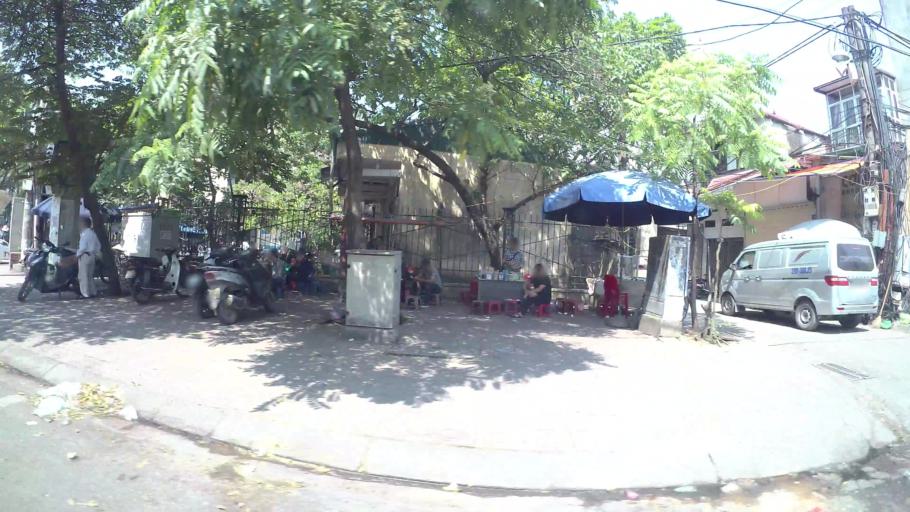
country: VN
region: Ha Noi
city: Hoan Kiem
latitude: 21.0502
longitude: 105.8773
